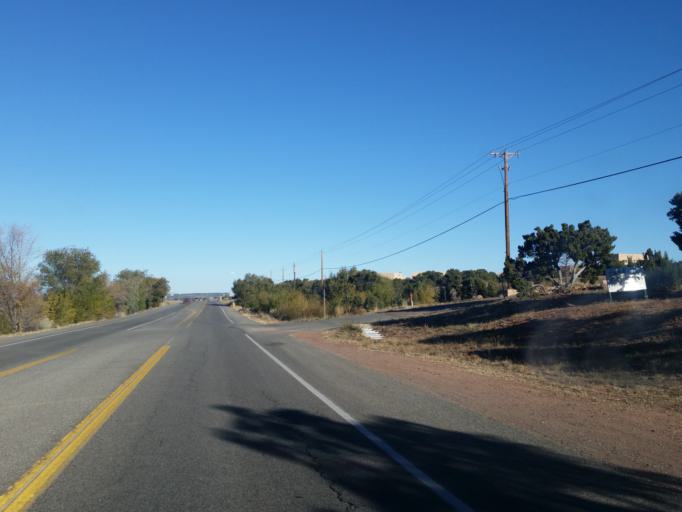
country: US
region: New Mexico
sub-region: Santa Fe County
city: Santa Fe
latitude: 35.6318
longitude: -105.9243
